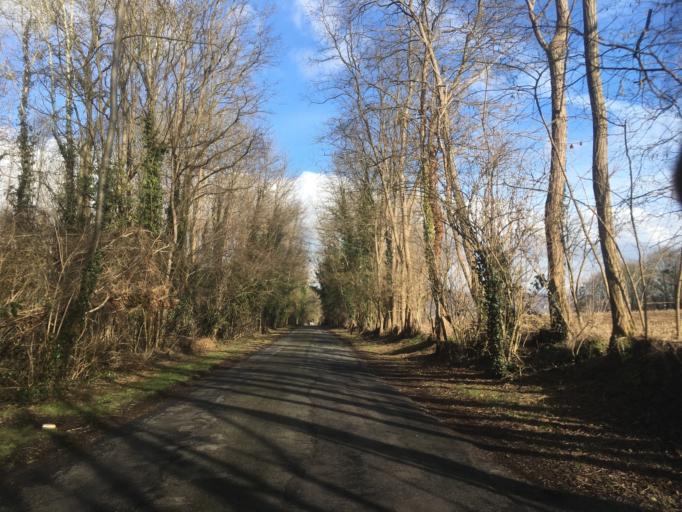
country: FR
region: Haute-Normandie
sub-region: Departement de l'Eure
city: Saint-Marcel
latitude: 49.0883
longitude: 1.4398
